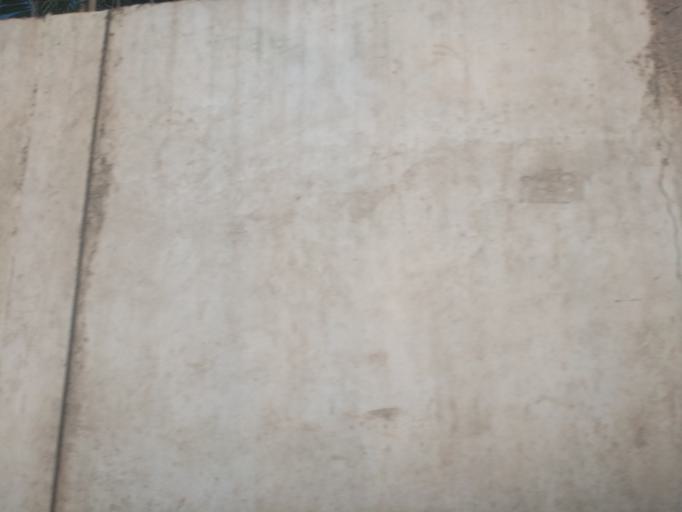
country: TZ
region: Pwani
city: Vikindu
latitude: -6.9225
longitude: 39.2680
